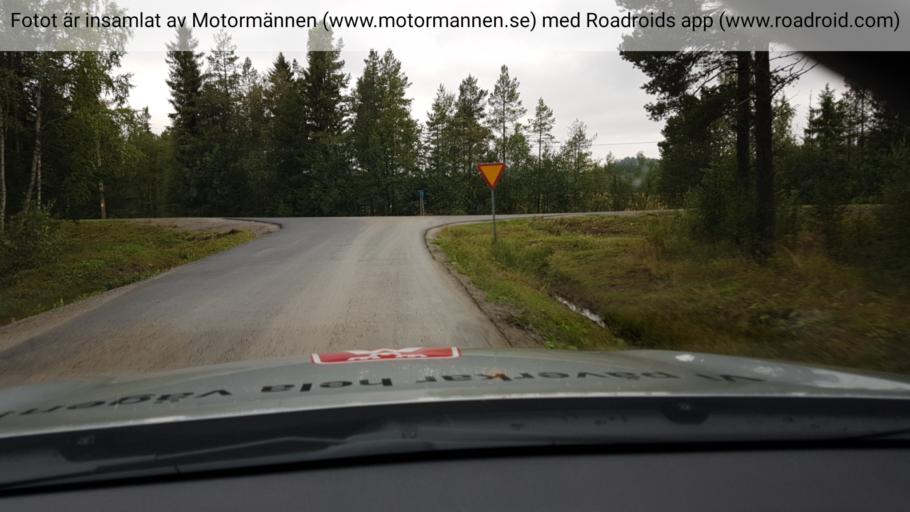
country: SE
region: Jaemtland
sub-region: Braecke Kommun
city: Braecke
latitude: 62.7808
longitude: 15.4715
